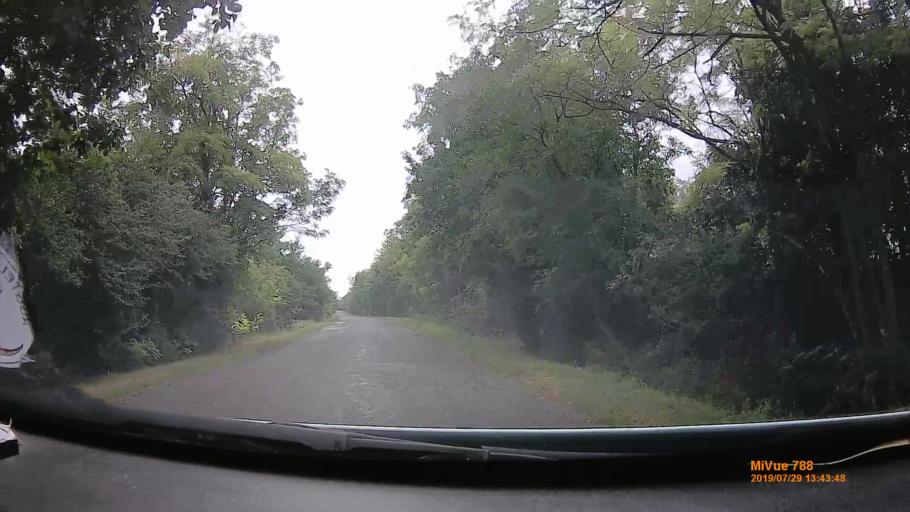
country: HU
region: Somogy
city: Balatonfoldvar
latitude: 46.8013
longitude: 17.9345
